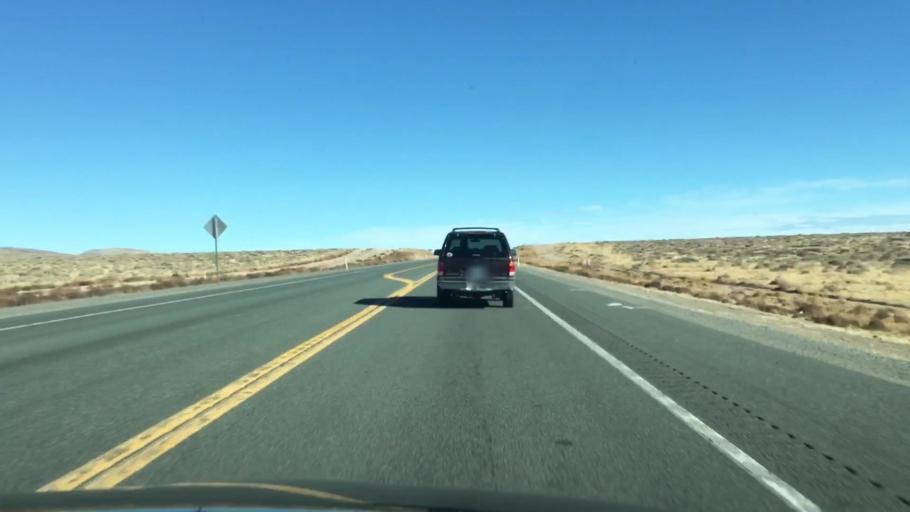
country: US
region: Nevada
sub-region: Lyon County
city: Stagecoach
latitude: 39.3691
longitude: -119.3534
